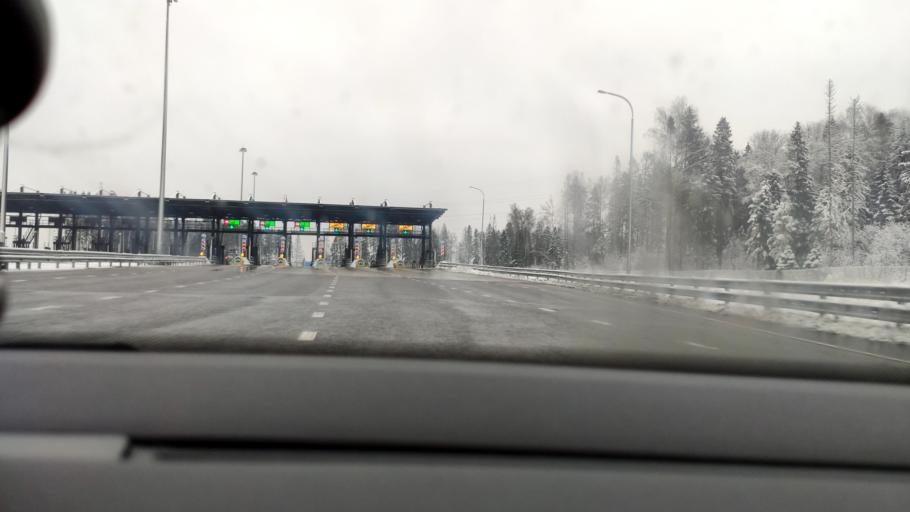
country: RU
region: Moskovskaya
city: Solnechnogorsk
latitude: 56.1602
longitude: 36.9144
